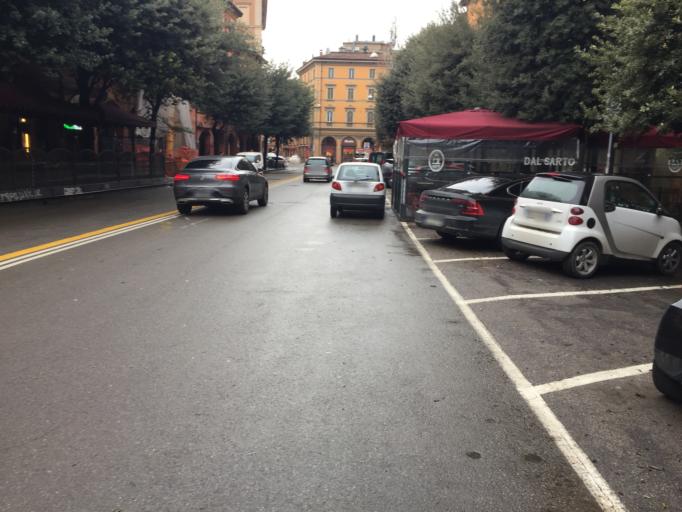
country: IT
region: Emilia-Romagna
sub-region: Provincia di Bologna
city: Bologna
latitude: 44.4990
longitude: 11.3452
